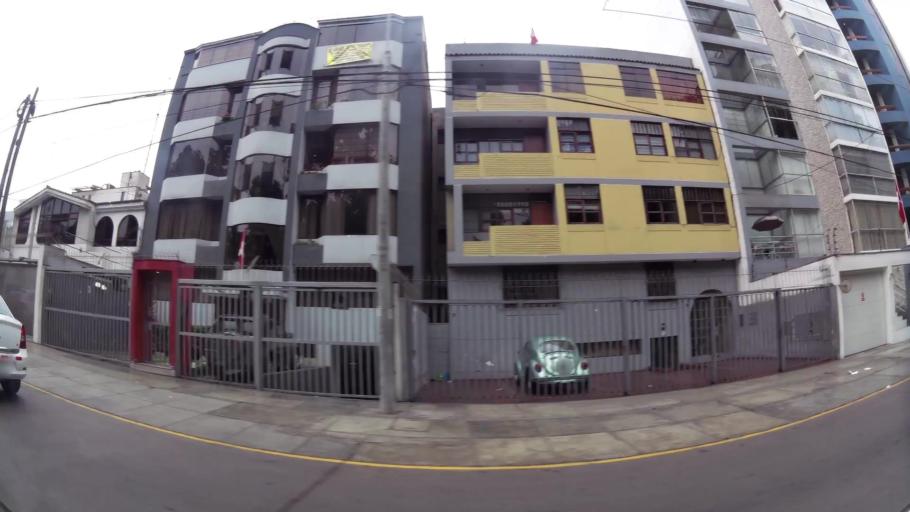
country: PE
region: Lima
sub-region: Lima
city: San Luis
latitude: -12.1014
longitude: -77.0050
